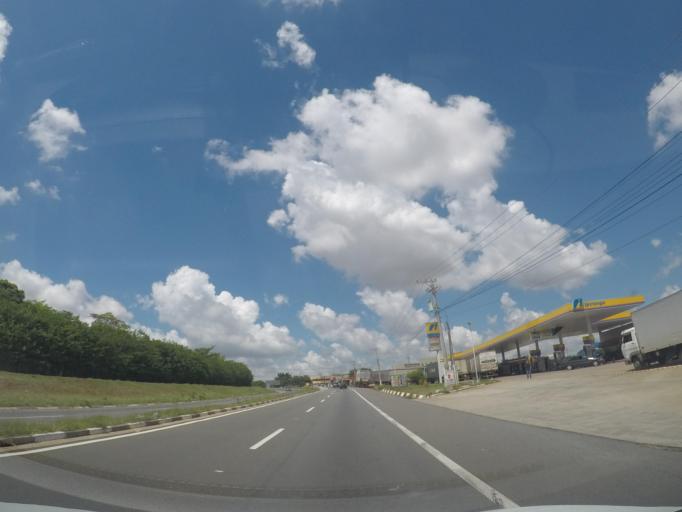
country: BR
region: Sao Paulo
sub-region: Hortolandia
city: Hortolandia
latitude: -22.8252
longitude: -47.1995
